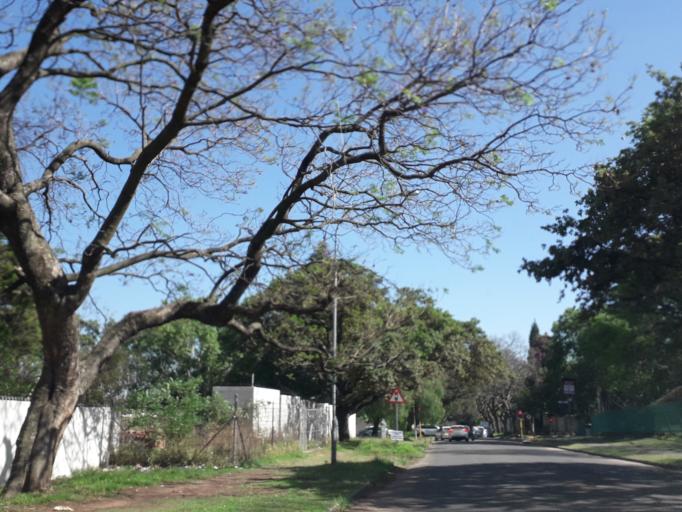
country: ZA
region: Gauteng
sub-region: City of Johannesburg Metropolitan Municipality
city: Johannesburg
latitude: -26.1567
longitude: 28.0619
